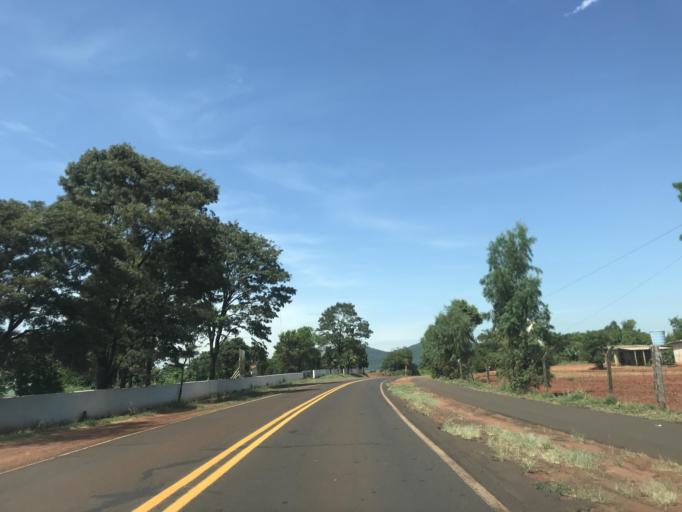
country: BR
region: Parana
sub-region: Terra Rica
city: Terra Rica
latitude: -22.7514
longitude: -52.6255
